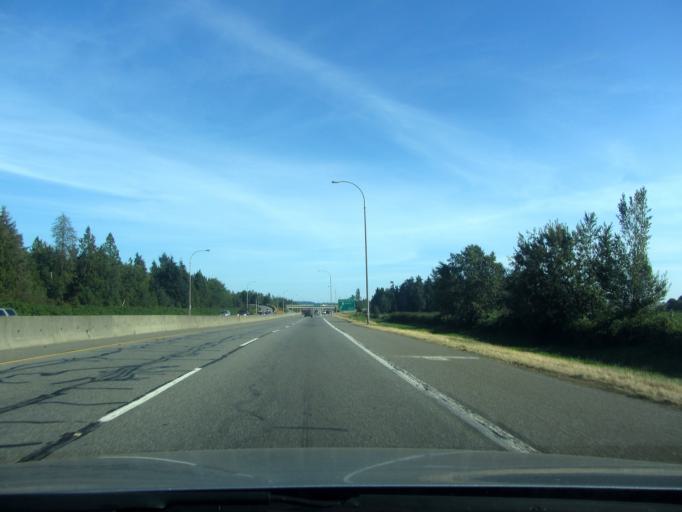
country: CA
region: British Columbia
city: Delta
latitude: 49.1079
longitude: -122.9038
